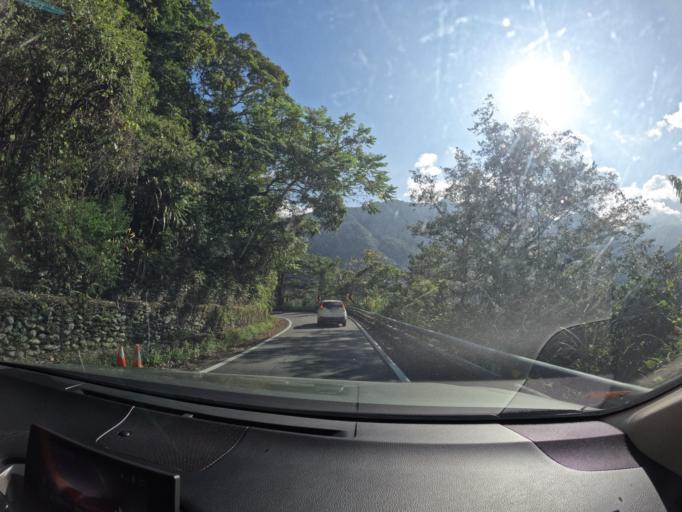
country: TW
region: Taiwan
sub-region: Taitung
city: Taitung
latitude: 23.1936
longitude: 121.0174
